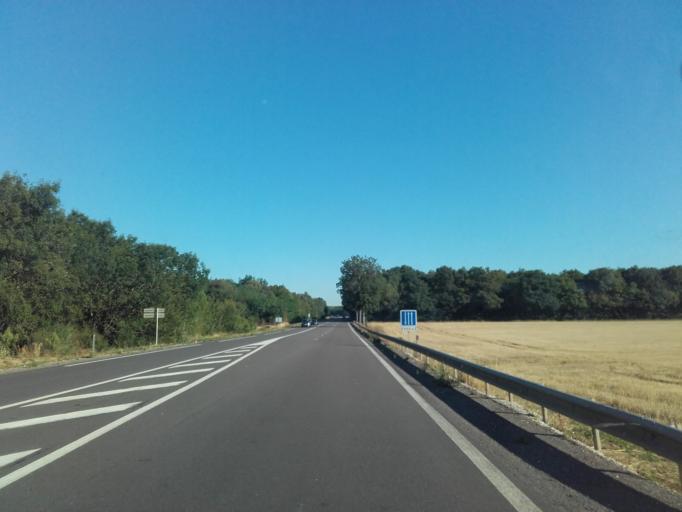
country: FR
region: Bourgogne
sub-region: Departement de Saone-et-Loire
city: Fontaines
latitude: 46.8660
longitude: 4.7941
